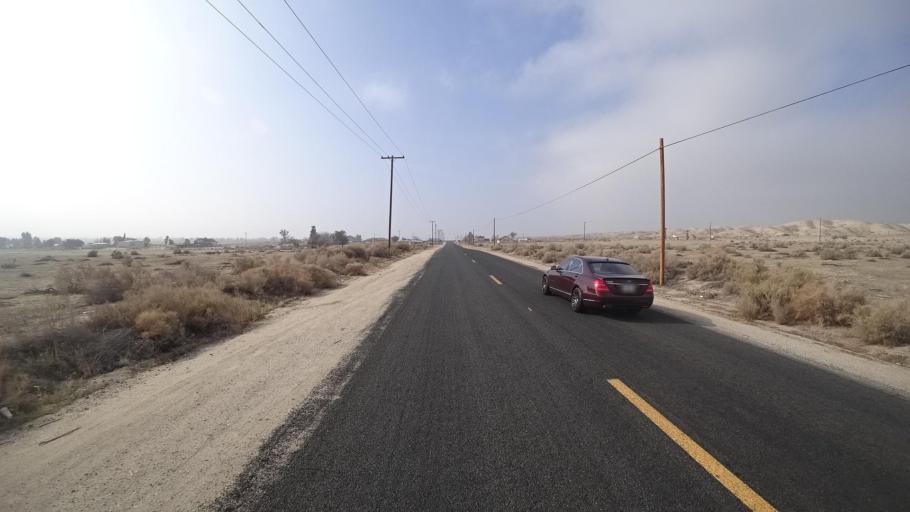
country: US
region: California
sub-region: Kern County
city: Ford City
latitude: 35.2323
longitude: -119.3655
